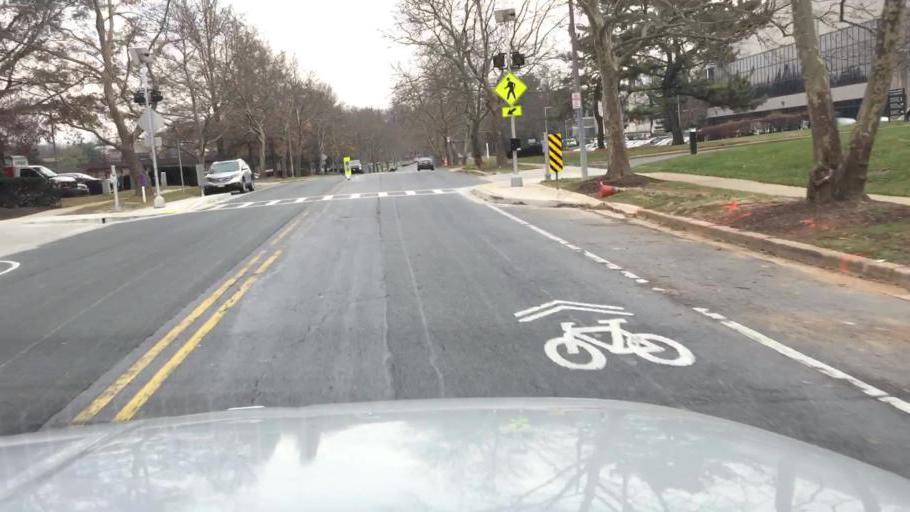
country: US
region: Maryland
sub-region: Montgomery County
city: Derwood
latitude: 39.1056
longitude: -77.1794
